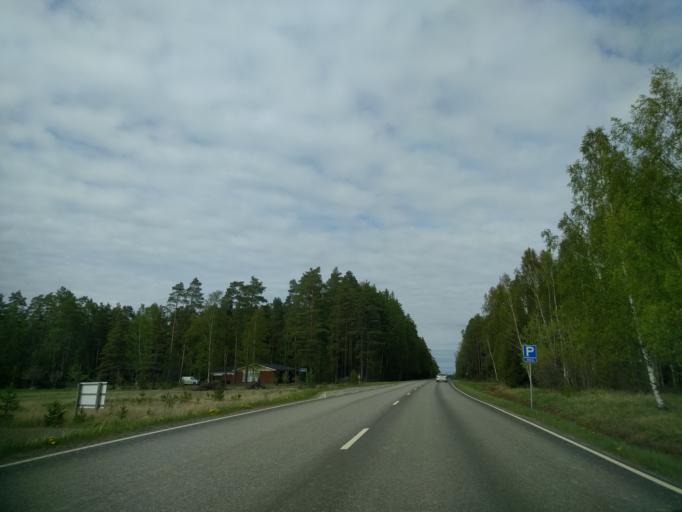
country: FI
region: Varsinais-Suomi
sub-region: Vakka-Suomi
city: Taivassalo
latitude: 60.5824
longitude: 21.6429
